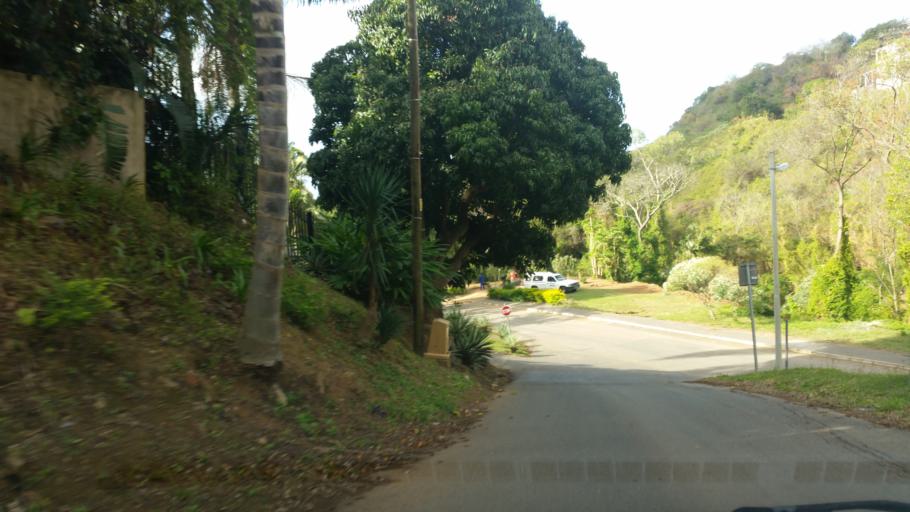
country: ZA
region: KwaZulu-Natal
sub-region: eThekwini Metropolitan Municipality
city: Berea
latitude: -29.8271
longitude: 30.9483
